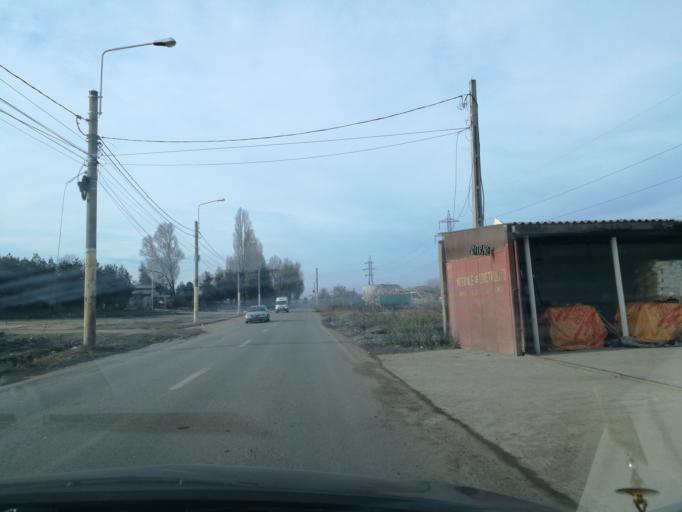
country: RO
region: Constanta
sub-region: Municipiul Constanta
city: Constanta
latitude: 44.1896
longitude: 28.6094
